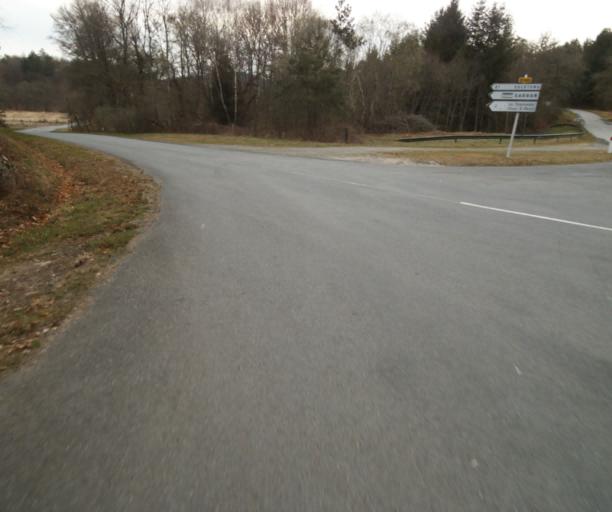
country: FR
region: Limousin
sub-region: Departement de la Correze
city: Correze
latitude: 45.4223
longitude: 1.8474
